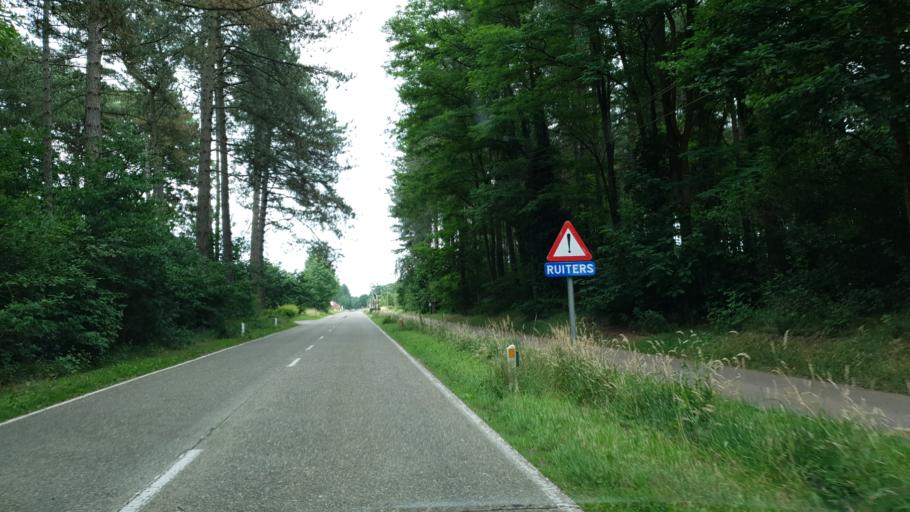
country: BE
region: Flanders
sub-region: Provincie Antwerpen
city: Westerlo
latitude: 51.0522
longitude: 4.9449
